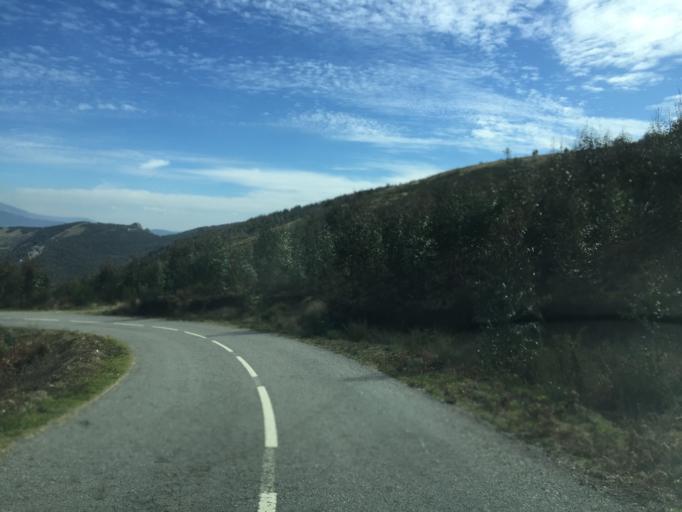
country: PT
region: Aveiro
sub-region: Arouca
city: Arouca
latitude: 40.9692
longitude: -8.2441
